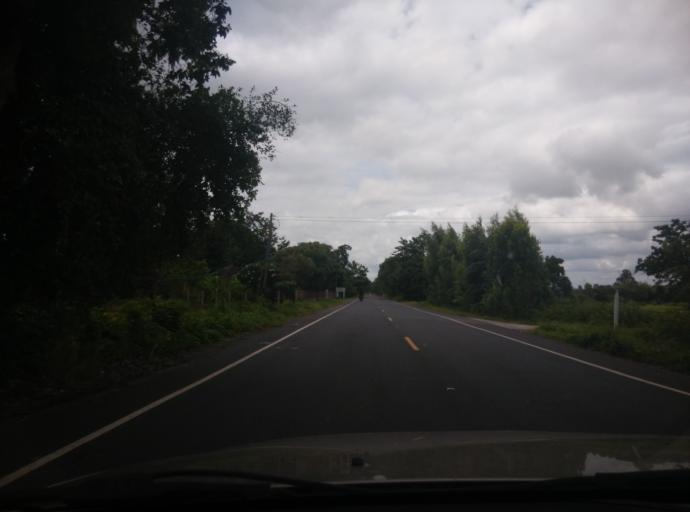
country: TH
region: Sisaket
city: Uthumphon Phisai
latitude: 15.1311
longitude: 104.1549
